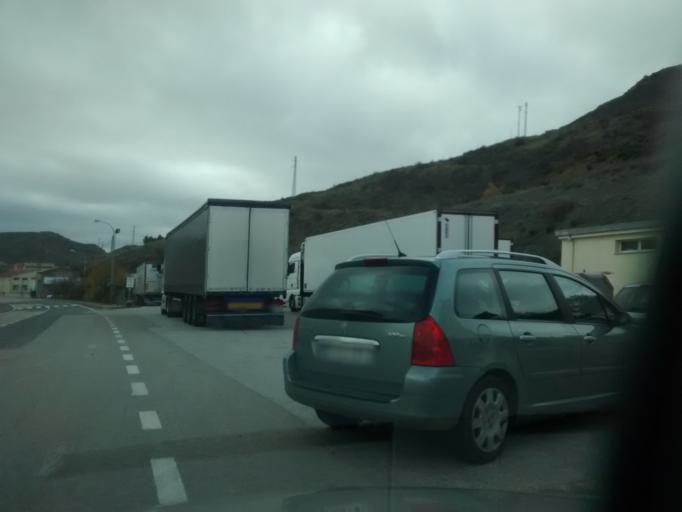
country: ES
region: Castille and Leon
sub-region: Provincia de Soria
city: Medinaceli
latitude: 41.1643
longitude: -2.4227
